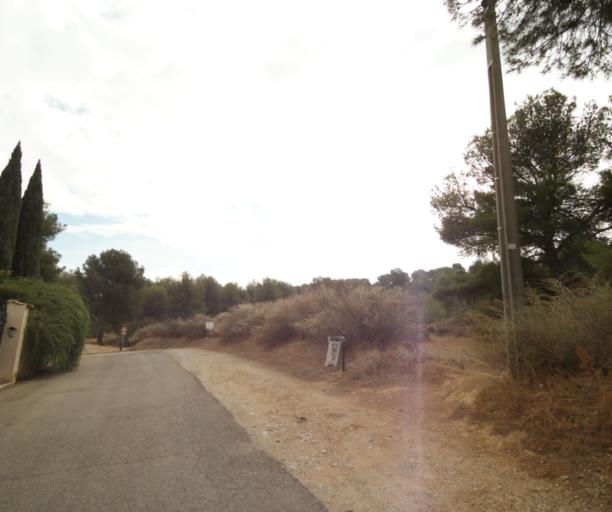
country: FR
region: Provence-Alpes-Cote d'Azur
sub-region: Departement des Bouches-du-Rhone
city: Saint-Victoret
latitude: 43.4102
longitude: 5.2647
